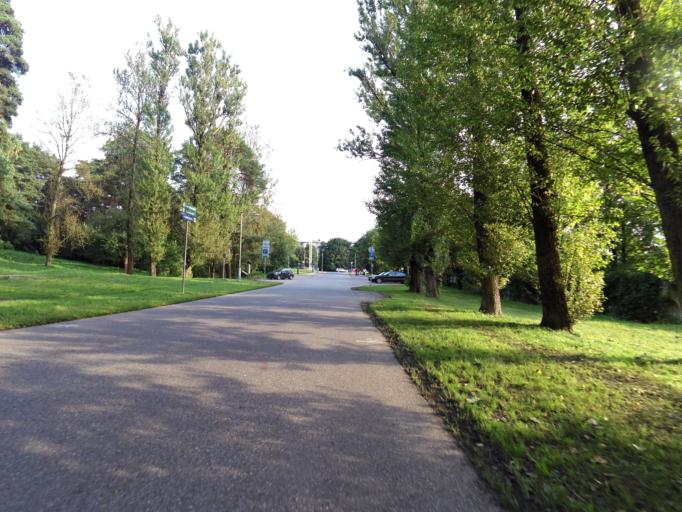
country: LT
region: Vilnius County
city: Vilkpede
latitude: 54.6745
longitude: 25.2393
